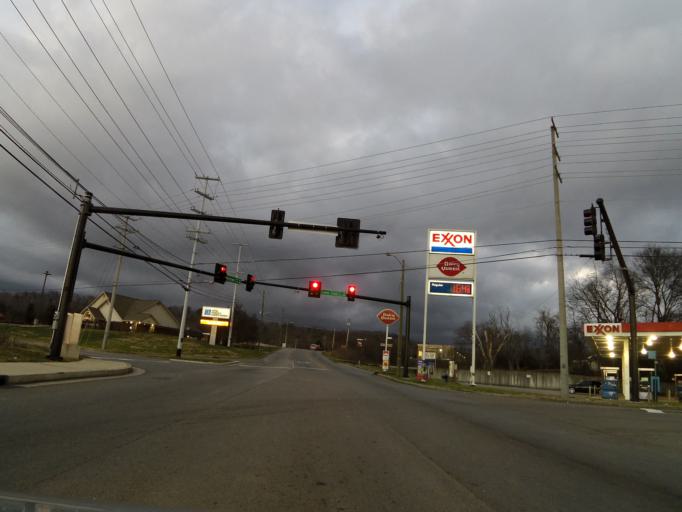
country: US
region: Tennessee
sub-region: Knox County
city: Knoxville
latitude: 36.0342
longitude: -83.8694
